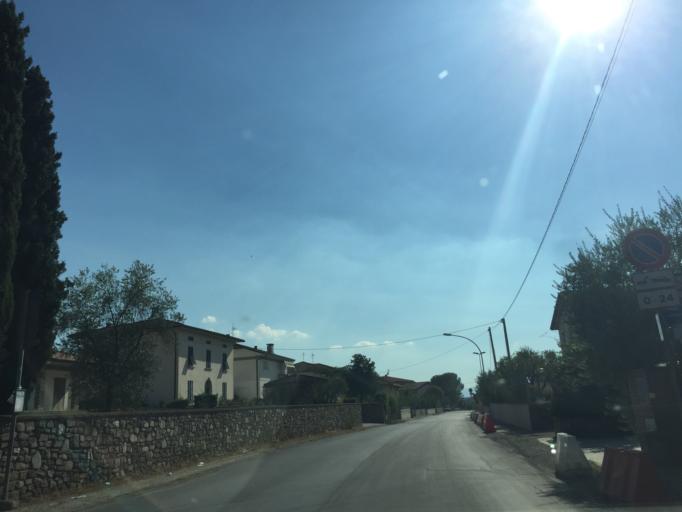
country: IT
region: Tuscany
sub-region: Provincia di Pistoia
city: San Rocco
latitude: 43.8186
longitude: 10.8635
